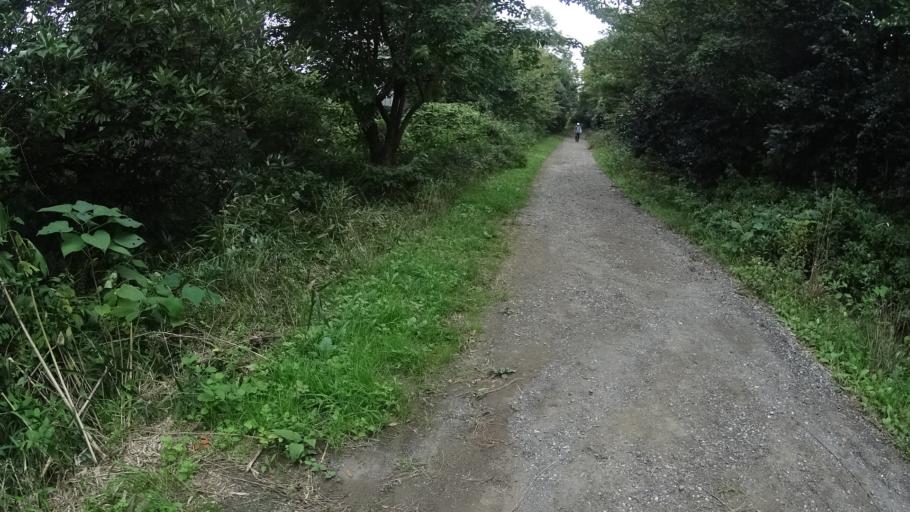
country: JP
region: Kanagawa
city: Zushi
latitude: 35.3513
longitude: 139.5961
